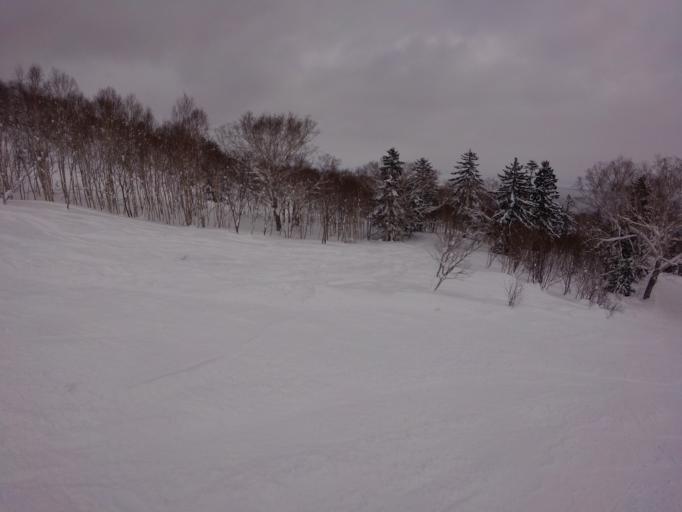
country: JP
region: Hokkaido
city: Sapporo
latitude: 43.0723
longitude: 141.2040
